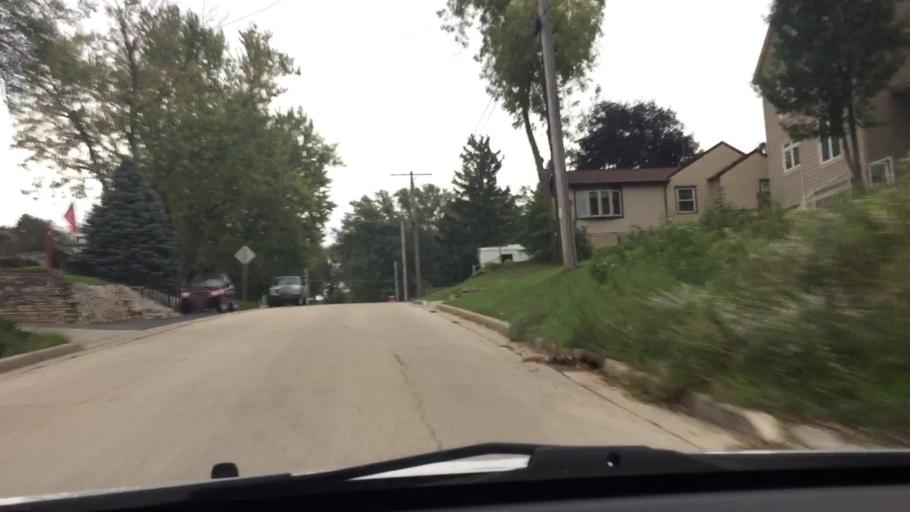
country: US
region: Wisconsin
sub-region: Waukesha County
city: Pewaukee
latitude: 43.0777
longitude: -88.2673
